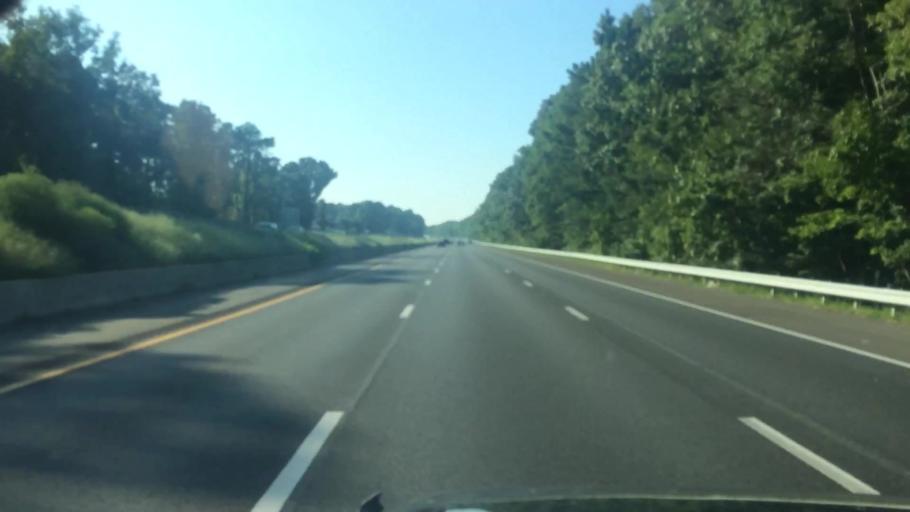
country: US
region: Virginia
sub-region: York County
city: Yorktown
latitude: 37.1520
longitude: -76.5363
